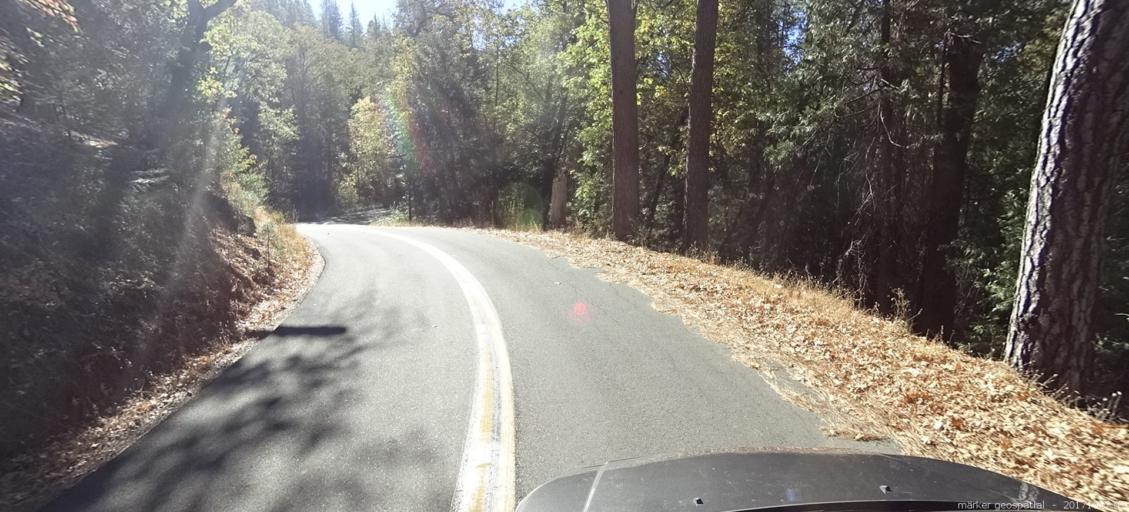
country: US
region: California
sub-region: Shasta County
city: Shingletown
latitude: 40.7406
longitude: -121.9522
